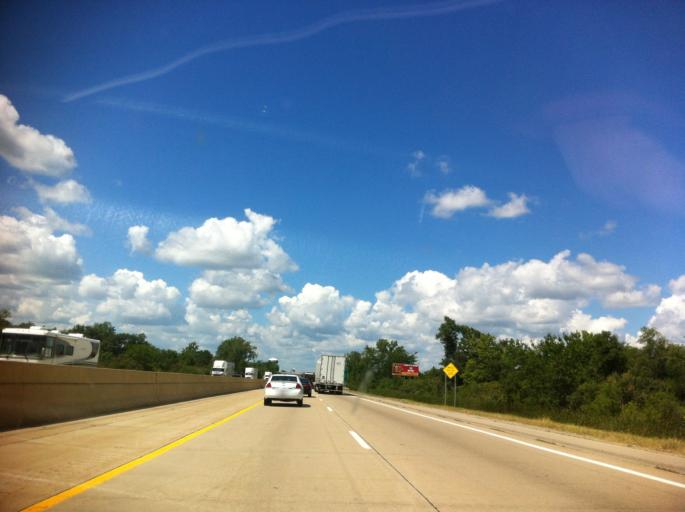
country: US
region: Michigan
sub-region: Monroe County
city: Dundee
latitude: 41.9434
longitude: -83.6645
